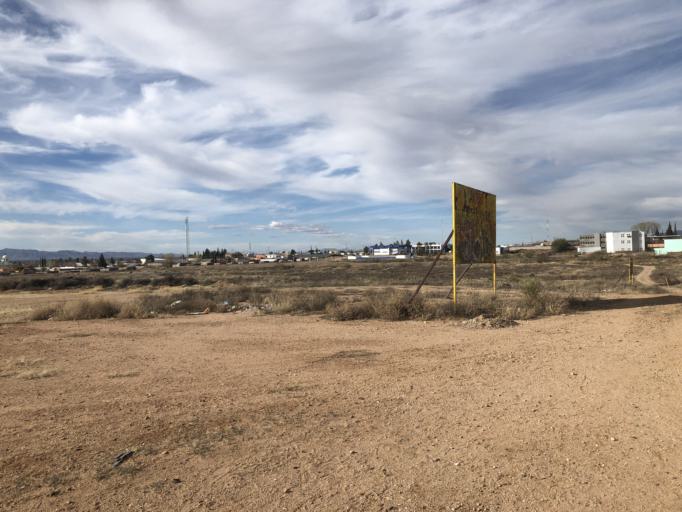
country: MX
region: Sonora
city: Agua Prieta
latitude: 31.3073
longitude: -109.5334
